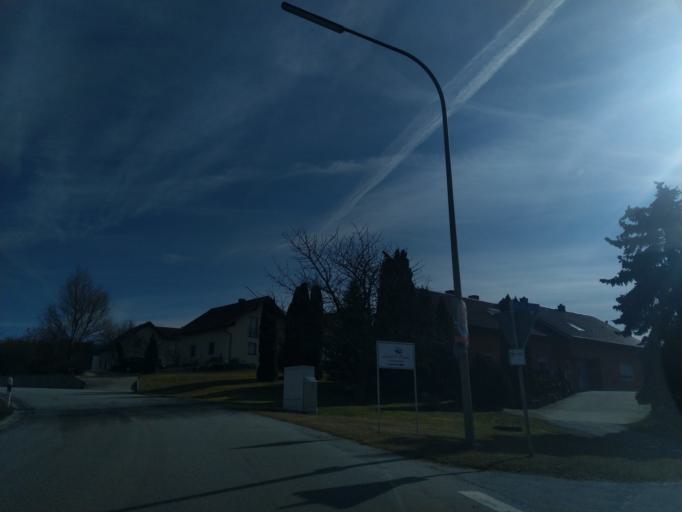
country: DE
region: Bavaria
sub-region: Lower Bavaria
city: Buchhofen
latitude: 48.6683
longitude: 12.9635
